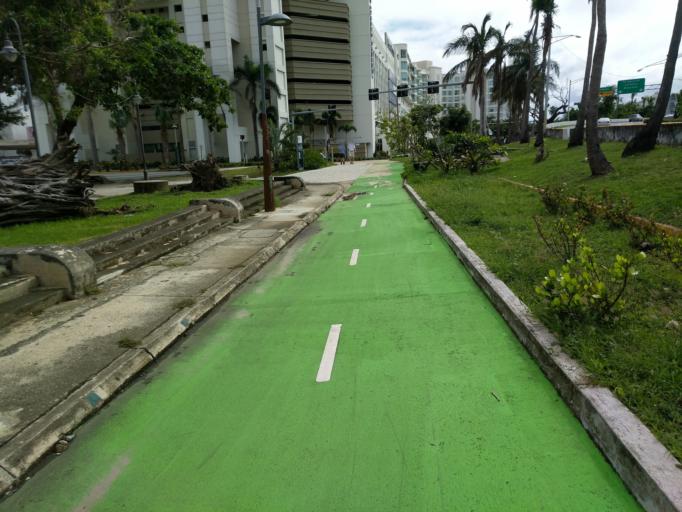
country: PR
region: San Juan
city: San Juan
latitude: 18.4625
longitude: -66.0885
